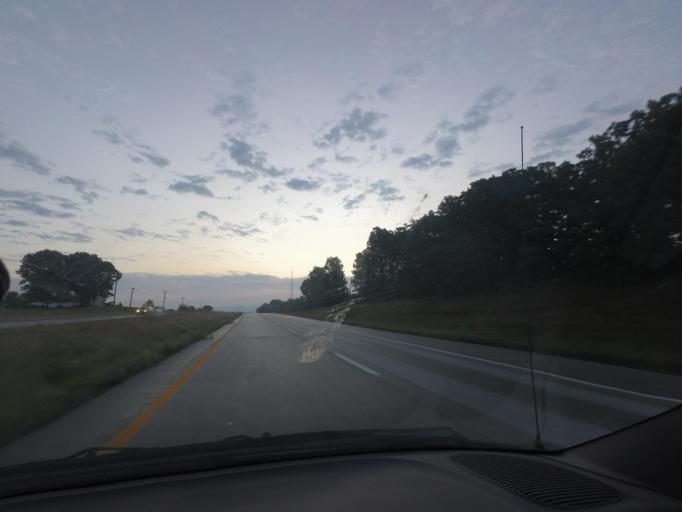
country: US
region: Missouri
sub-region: Macon County
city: Macon
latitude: 39.7488
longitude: -92.4832
